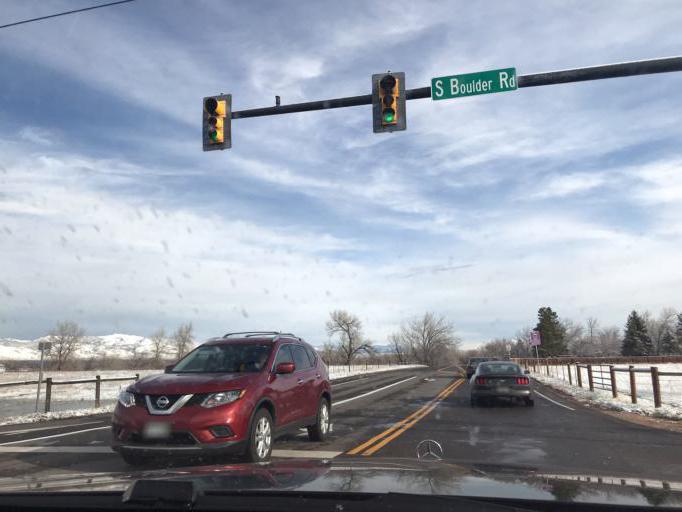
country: US
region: Colorado
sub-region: Boulder County
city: Superior
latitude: 39.9861
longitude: -105.2128
